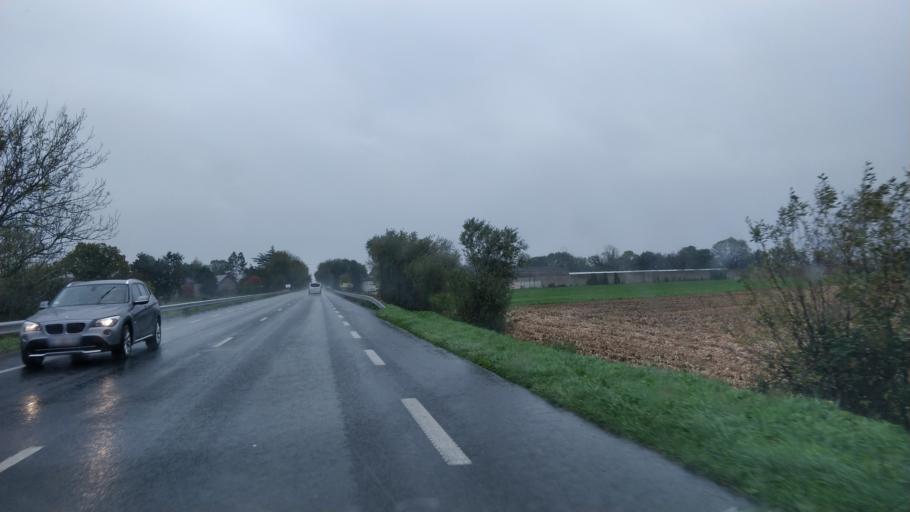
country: FR
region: Lower Normandy
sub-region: Departement de la Manche
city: Brehal
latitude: 48.8771
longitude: -1.5334
